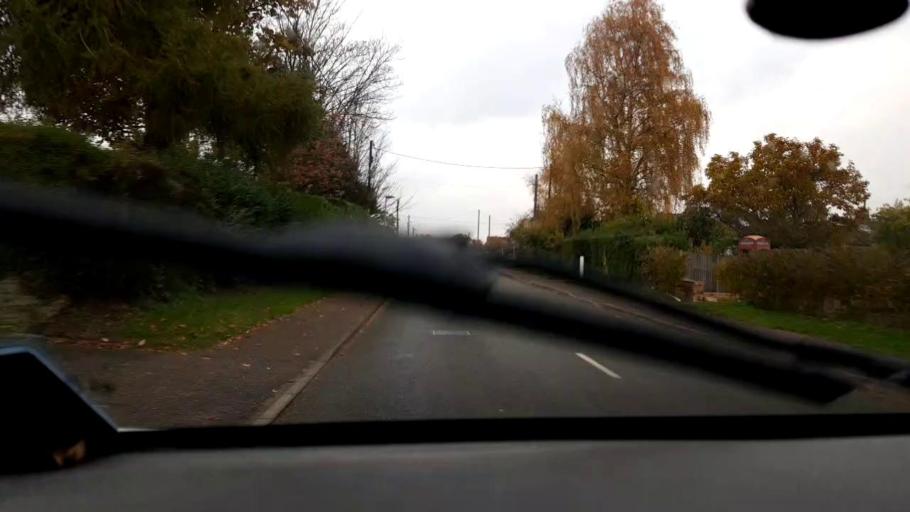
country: GB
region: England
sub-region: Norfolk
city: Spixworth
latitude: 52.6877
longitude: 1.3220
